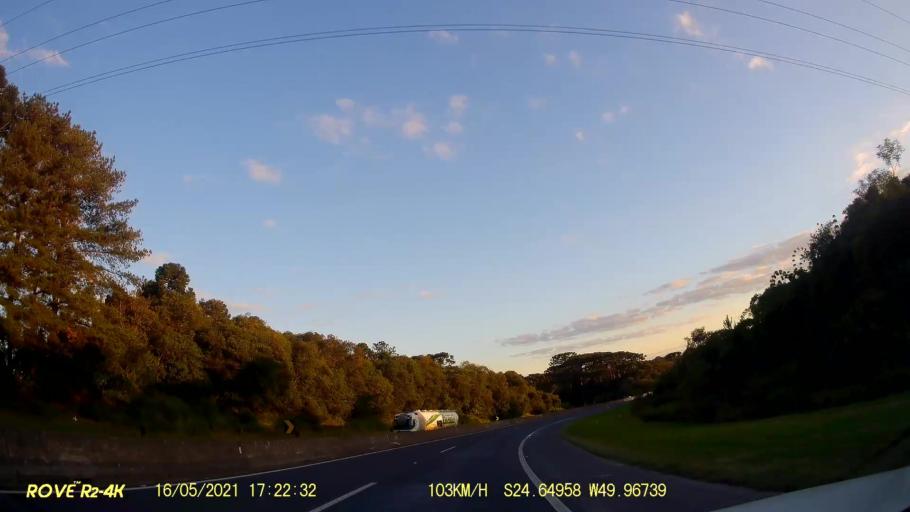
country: BR
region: Parana
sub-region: Pirai Do Sul
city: Pirai do Sul
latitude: -24.6500
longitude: -49.9673
